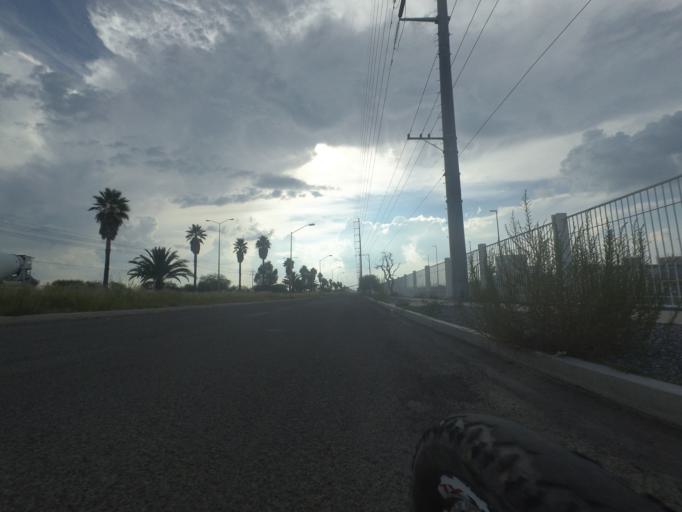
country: MX
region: Aguascalientes
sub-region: Aguascalientes
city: Penuelas (El Cienegal)
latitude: 21.7252
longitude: -102.2951
